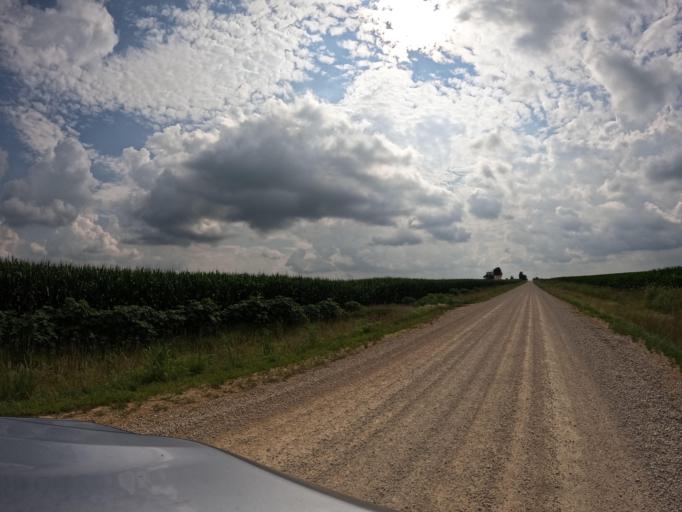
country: US
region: Iowa
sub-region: Clinton County
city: Camanche
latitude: 41.8012
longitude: -90.3742
